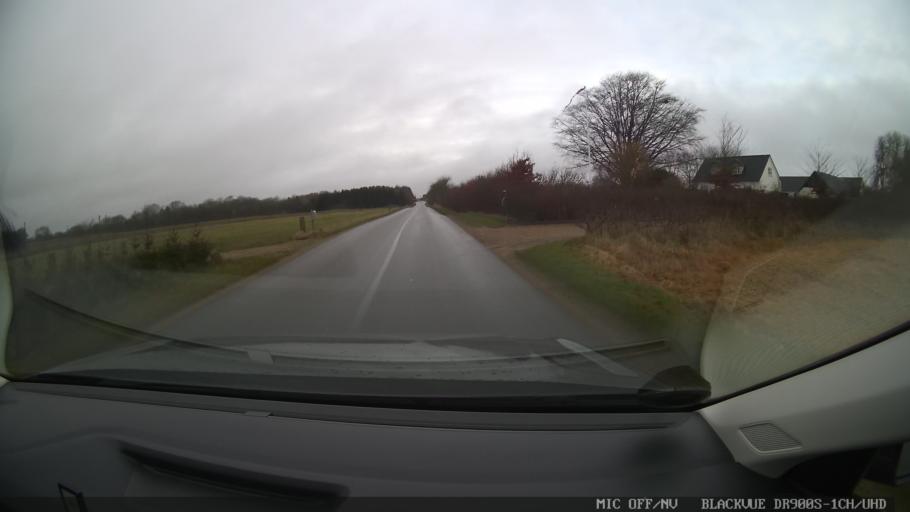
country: DK
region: Central Jutland
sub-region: Viborg Kommune
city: Karup
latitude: 56.3514
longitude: 9.2899
